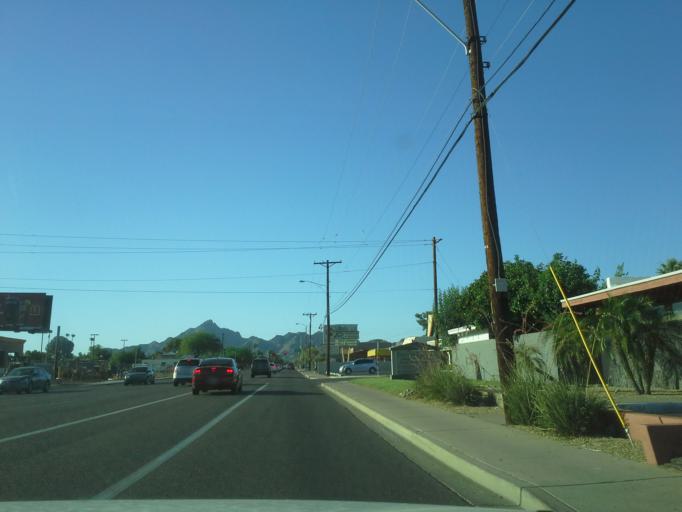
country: US
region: Arizona
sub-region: Maricopa County
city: Phoenix
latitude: 33.4927
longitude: -112.0129
